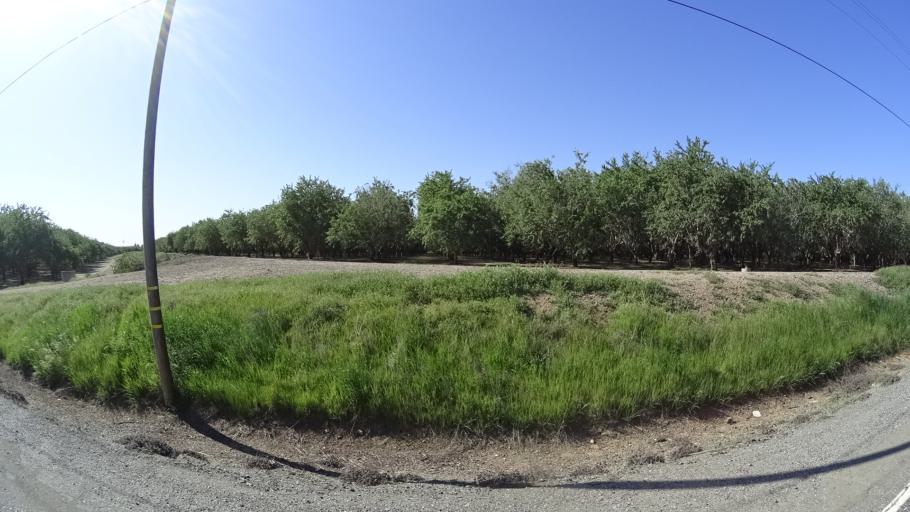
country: US
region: California
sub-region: Glenn County
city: Hamilton City
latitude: 39.7091
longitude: -122.0427
